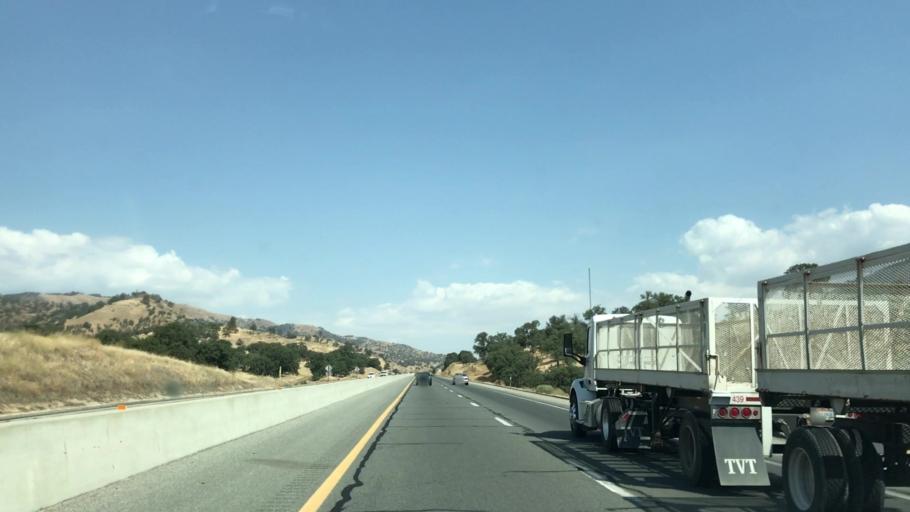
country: US
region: California
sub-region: Kern County
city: Golden Hills
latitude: 35.2136
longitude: -118.5485
